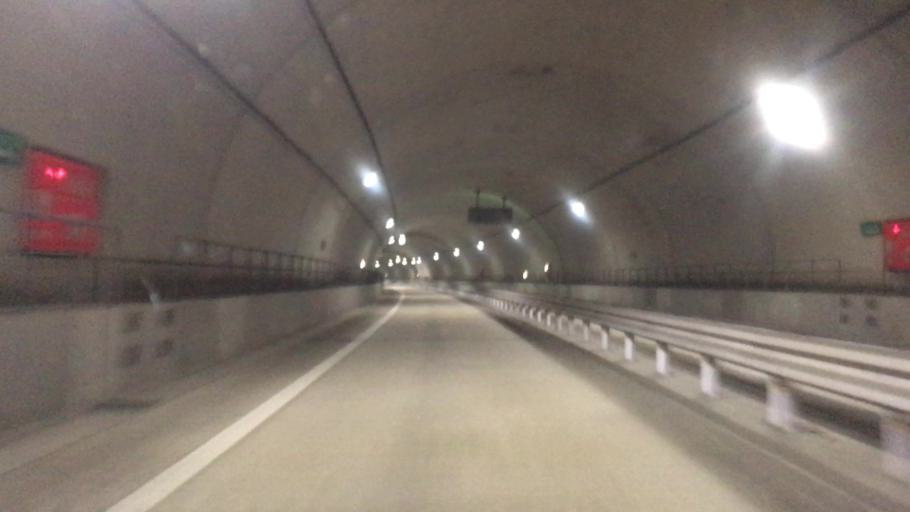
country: JP
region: Tottori
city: Tottori
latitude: 35.5741
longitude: 134.3228
